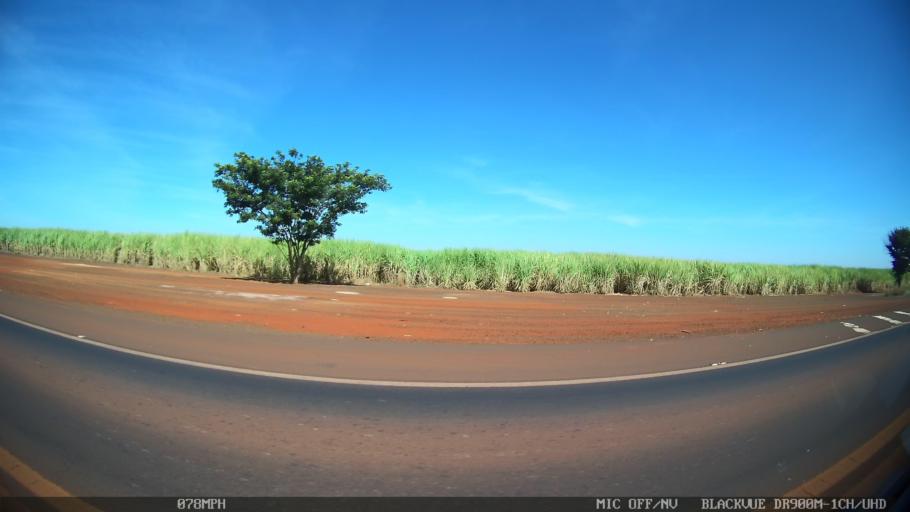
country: BR
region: Sao Paulo
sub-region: Sao Joaquim Da Barra
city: Sao Joaquim da Barra
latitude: -20.5439
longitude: -47.7887
